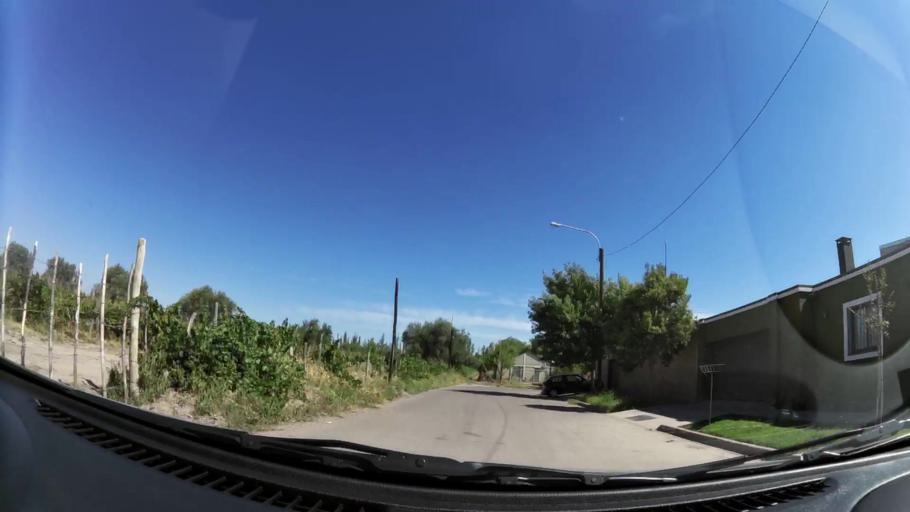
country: AR
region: Mendoza
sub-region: Departamento de Godoy Cruz
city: Godoy Cruz
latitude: -32.9735
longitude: -68.8351
